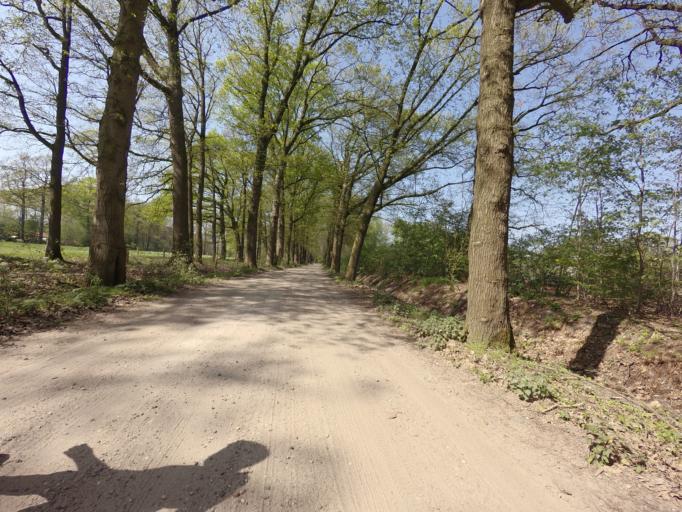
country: NL
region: North Brabant
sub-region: Gemeente Baarle-Nassau
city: Baarle-Nassau
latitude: 51.4858
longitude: 4.9947
